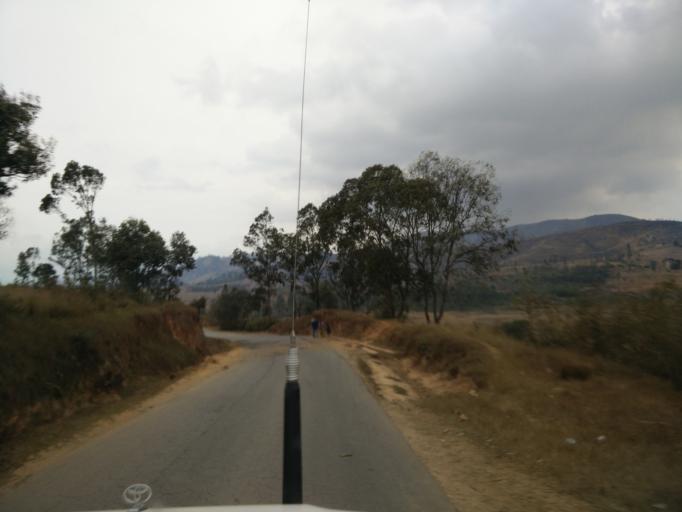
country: MG
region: Upper Matsiatra
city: Fianarantsoa
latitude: -21.5921
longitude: 47.0123
